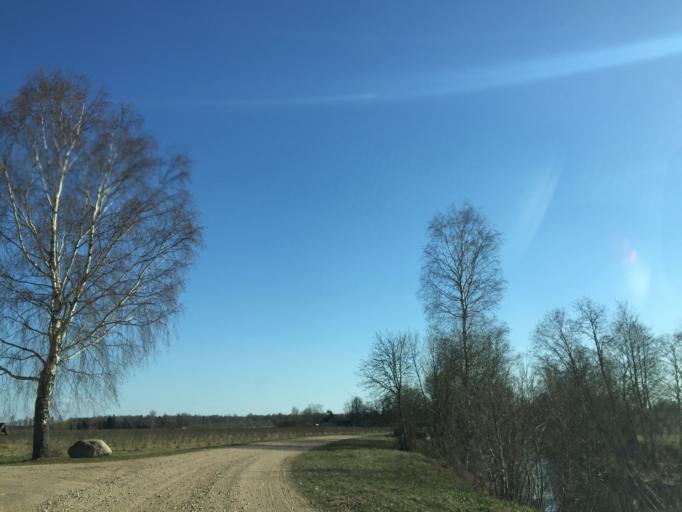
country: EE
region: Valgamaa
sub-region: Torva linn
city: Torva
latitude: 58.2441
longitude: 25.9269
